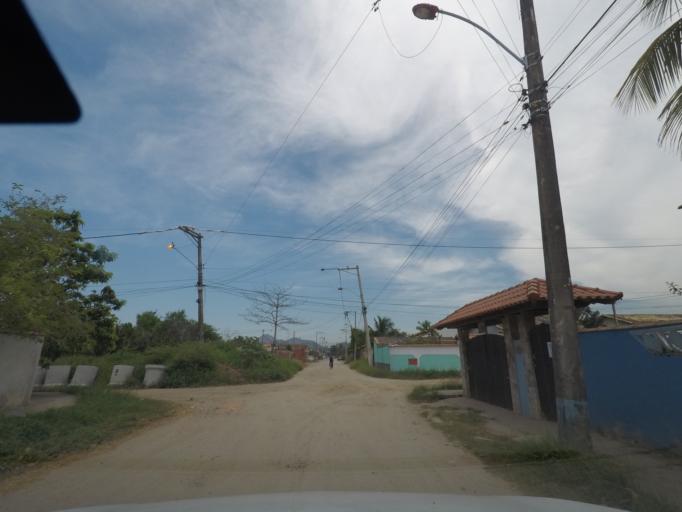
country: BR
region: Rio de Janeiro
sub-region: Marica
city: Marica
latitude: -22.9620
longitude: -42.9557
